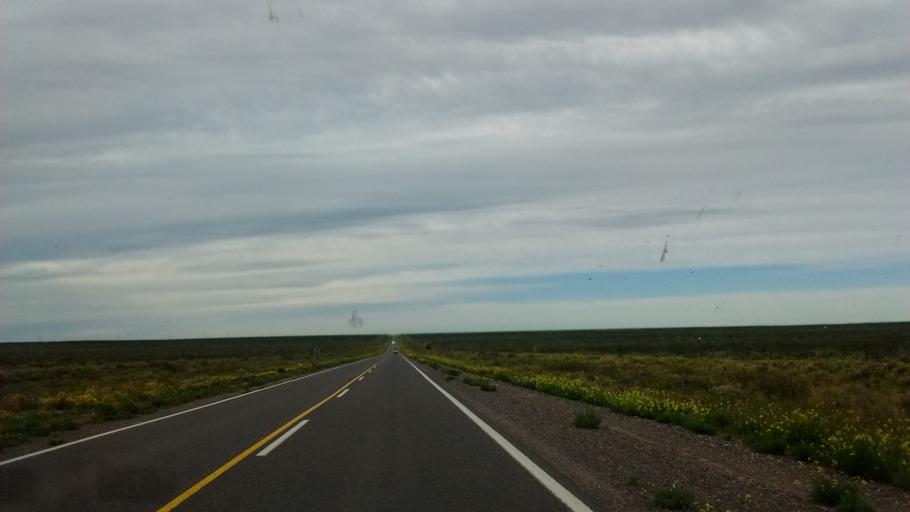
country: AR
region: Rio Negro
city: Catriel
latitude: -38.2362
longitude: -67.9836
